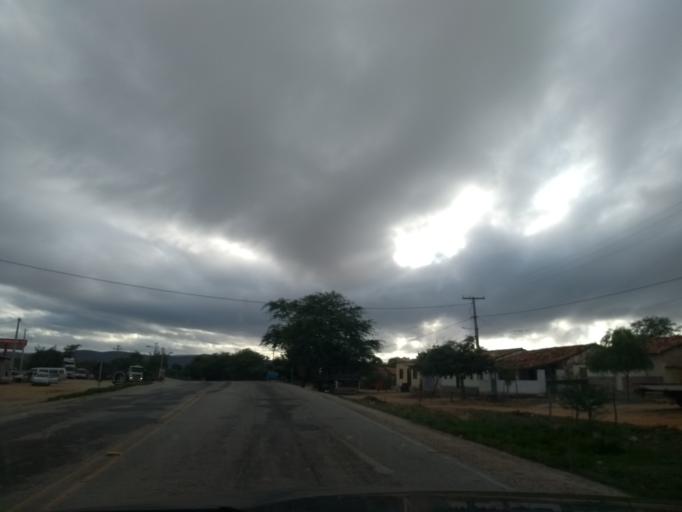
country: BR
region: Bahia
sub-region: Ituacu
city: Ituacu
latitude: -13.7608
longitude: -41.0326
